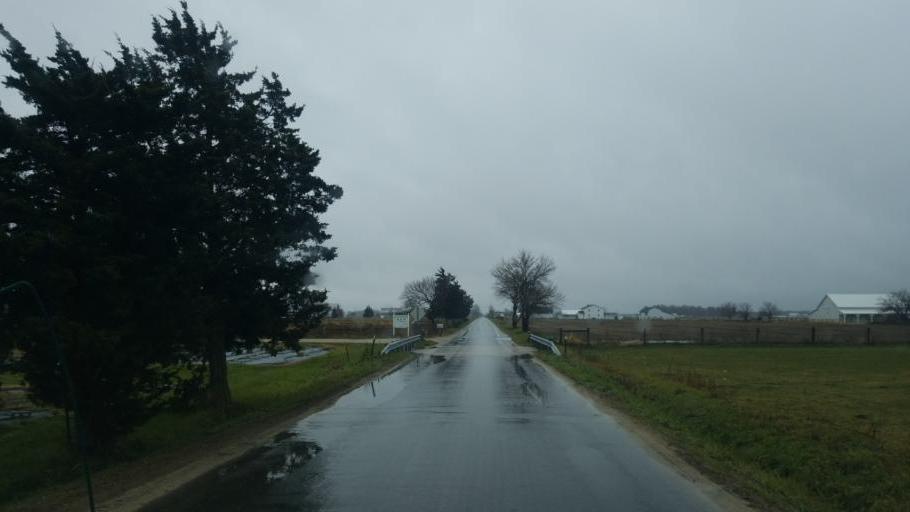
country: US
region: Indiana
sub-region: Adams County
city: Berne
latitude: 40.7159
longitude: -84.9174
